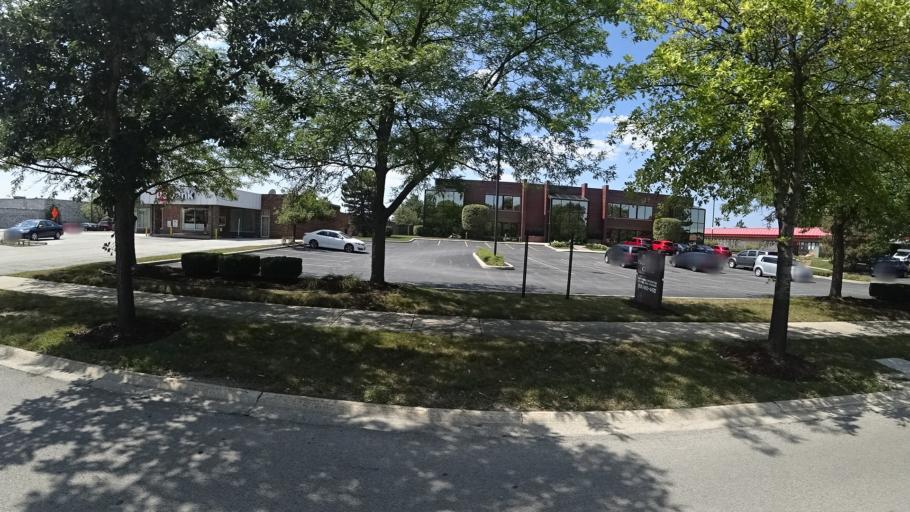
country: US
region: Illinois
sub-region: Cook County
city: Orland Park
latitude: 41.6239
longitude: -87.8514
